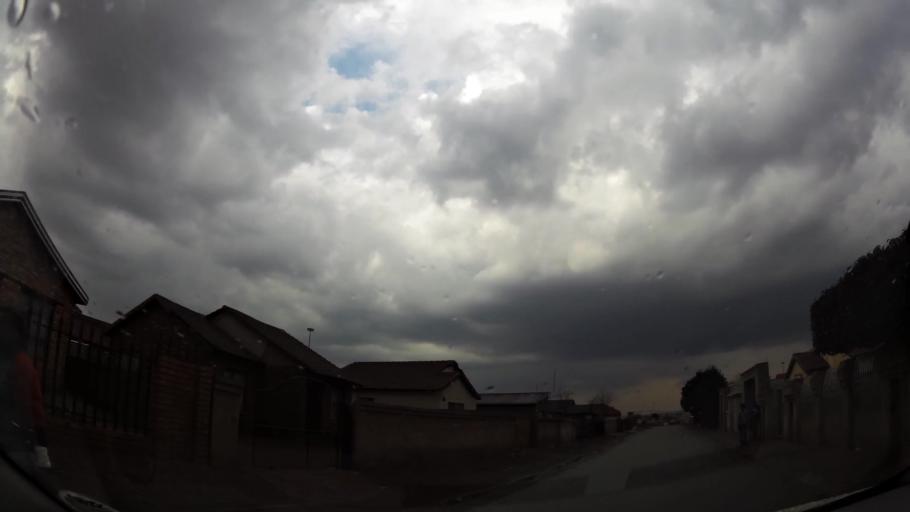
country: ZA
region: Gauteng
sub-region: Ekurhuleni Metropolitan Municipality
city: Germiston
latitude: -26.3669
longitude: 28.1357
